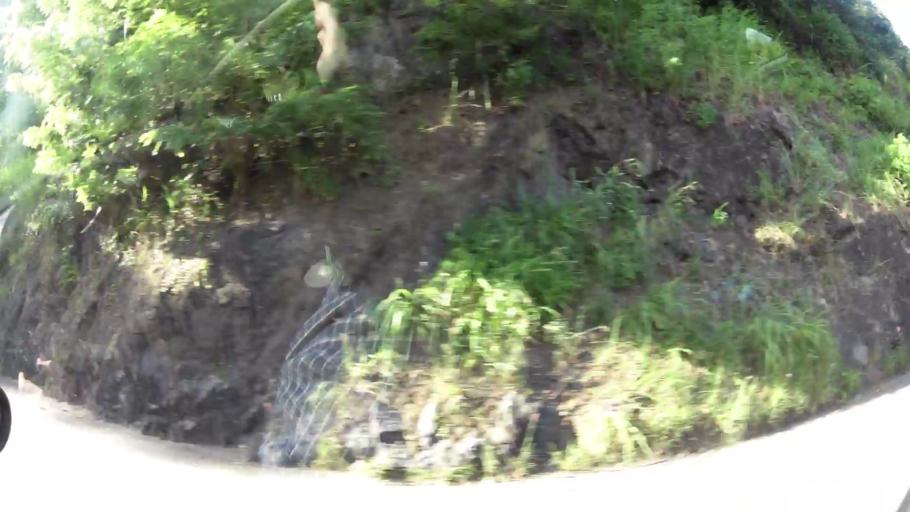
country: TT
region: Eastern Tobago
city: Roxborough
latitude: 11.2324
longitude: -60.6067
